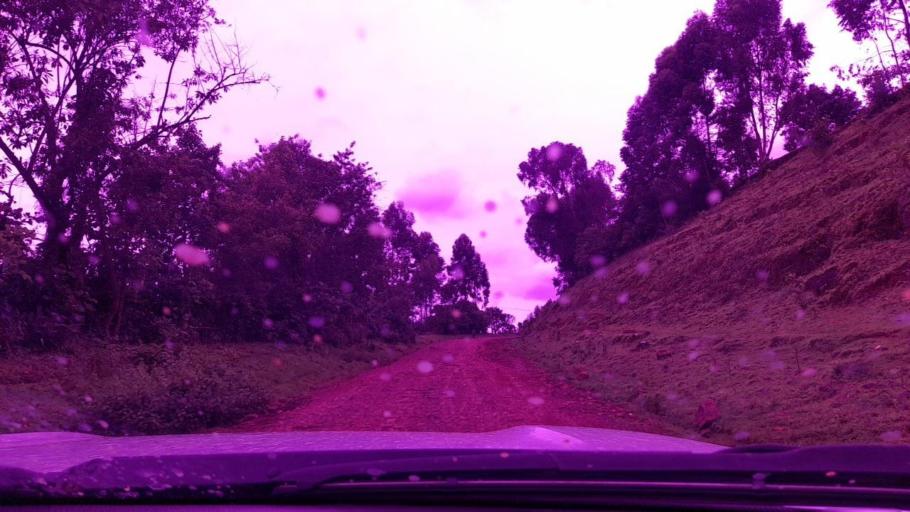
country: ET
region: Southern Nations, Nationalities, and People's Region
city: Tippi
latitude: 7.5683
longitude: 35.6515
